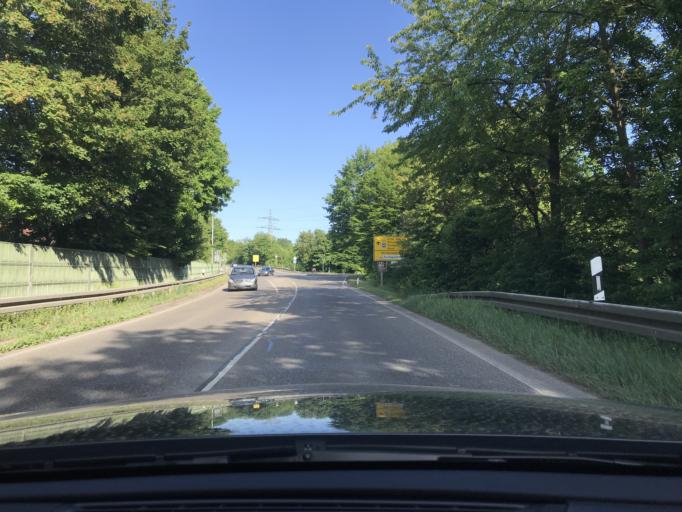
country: DE
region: Baden-Wuerttemberg
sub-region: Regierungsbezirk Stuttgart
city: Waiblingen
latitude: 48.8295
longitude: 9.3276
